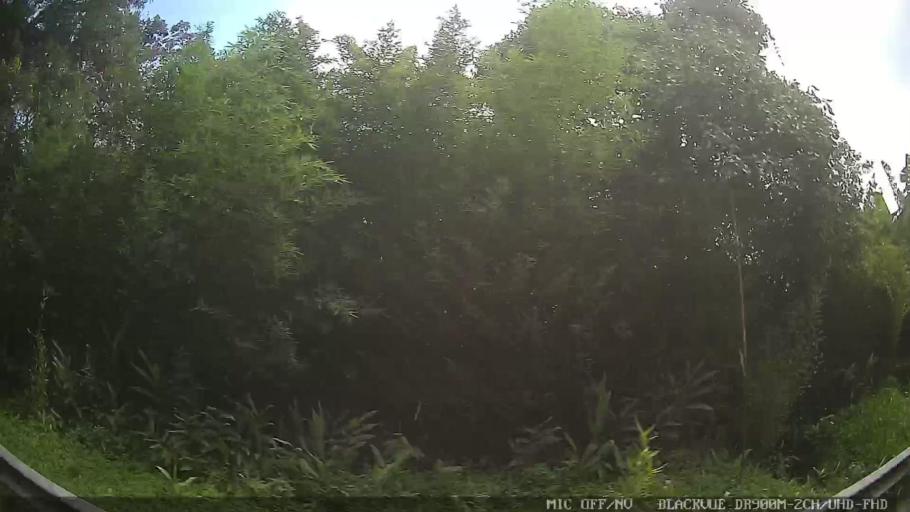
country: BR
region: Sao Paulo
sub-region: Ribeirao Pires
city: Ribeirao Pires
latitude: -23.6869
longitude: -46.3832
